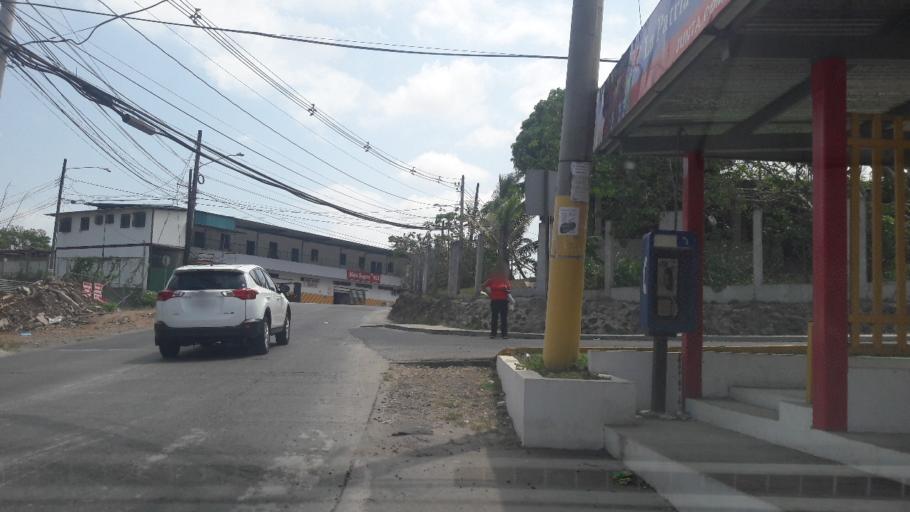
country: PA
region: Panama
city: La Cabima
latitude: 9.1238
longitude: -79.5446
